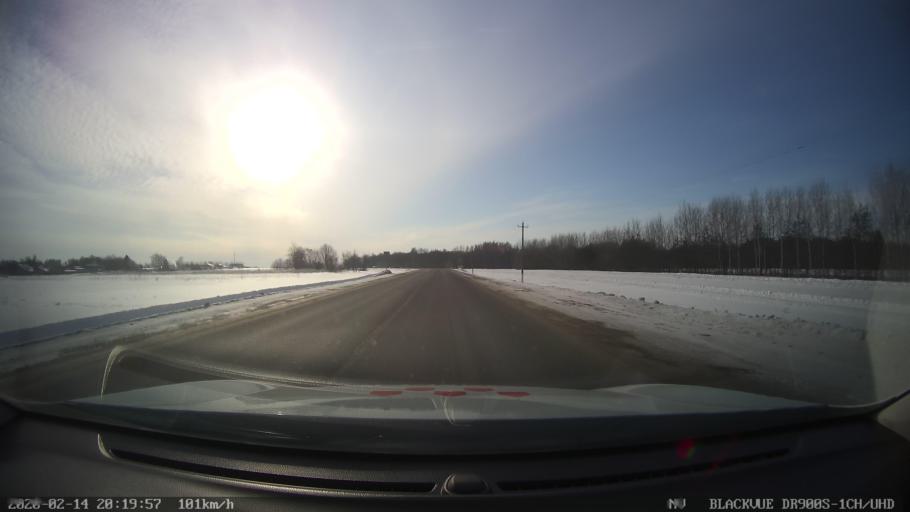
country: RU
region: Tatarstan
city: Verkhniy Uslon
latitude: 55.5629
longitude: 48.9017
